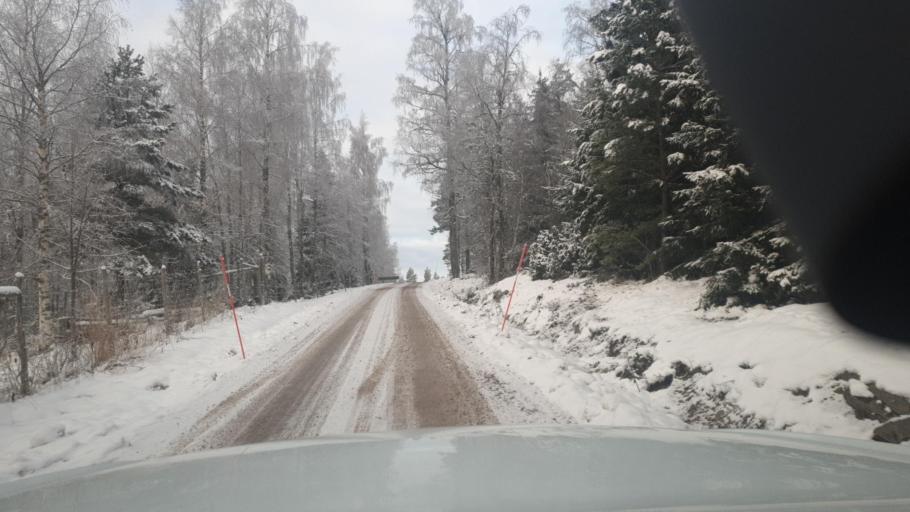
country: SE
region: Vaermland
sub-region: Torsby Kommun
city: Torsby
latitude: 59.9456
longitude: 12.7963
